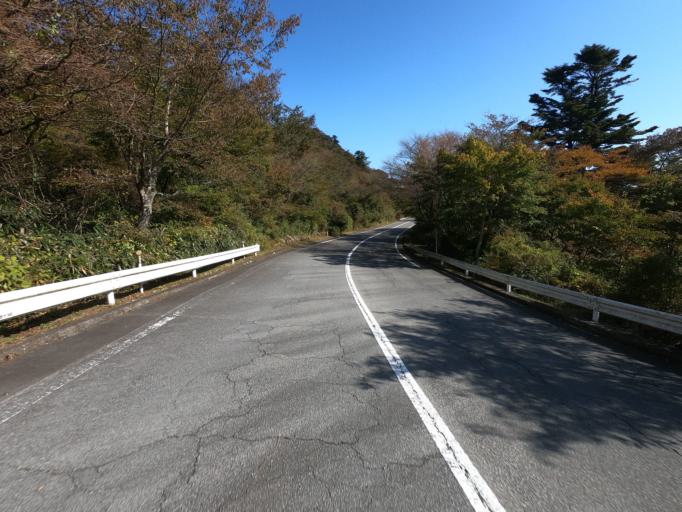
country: JP
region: Kanagawa
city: Hakone
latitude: 35.2022
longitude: 139.0850
